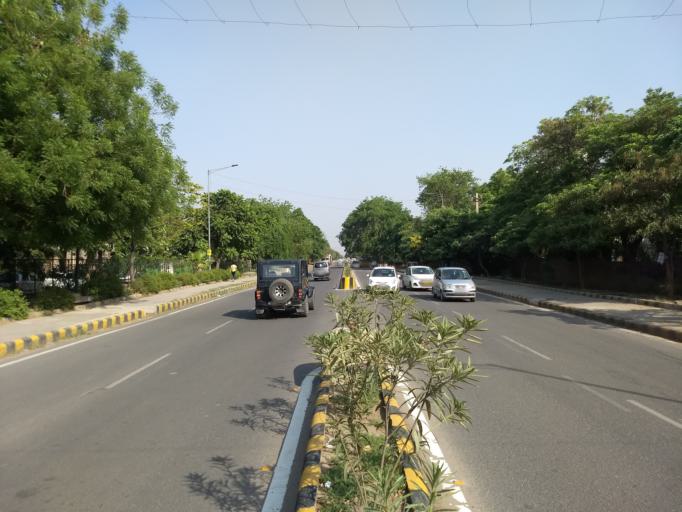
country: IN
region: Haryana
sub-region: Gurgaon
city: Gurgaon
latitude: 28.4418
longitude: 77.0606
